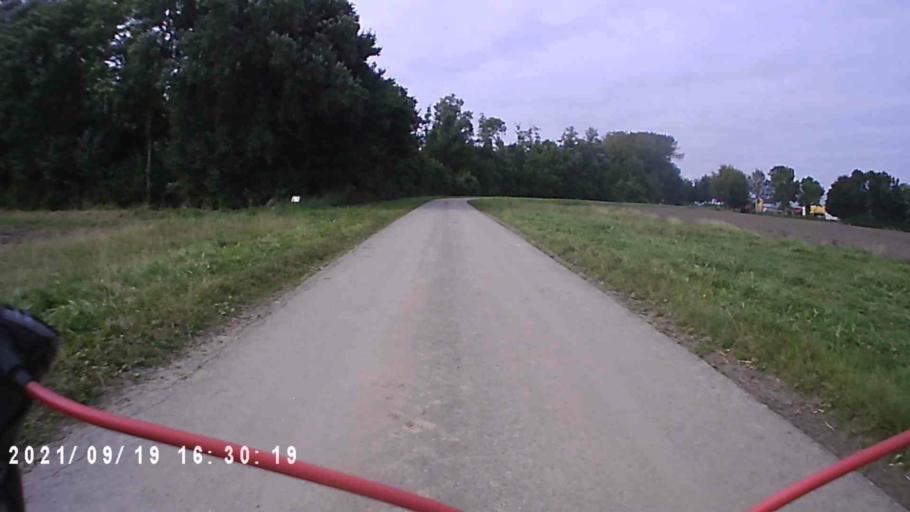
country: DE
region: Lower Saxony
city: Bunde
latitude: 53.1857
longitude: 7.1675
